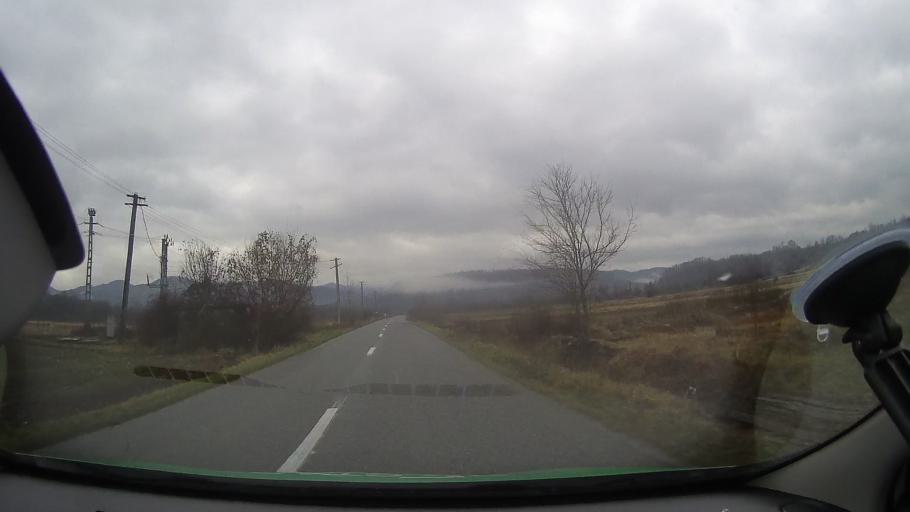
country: RO
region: Arad
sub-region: Comuna Brazii
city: Brazii
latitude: 46.2448
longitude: 22.3311
